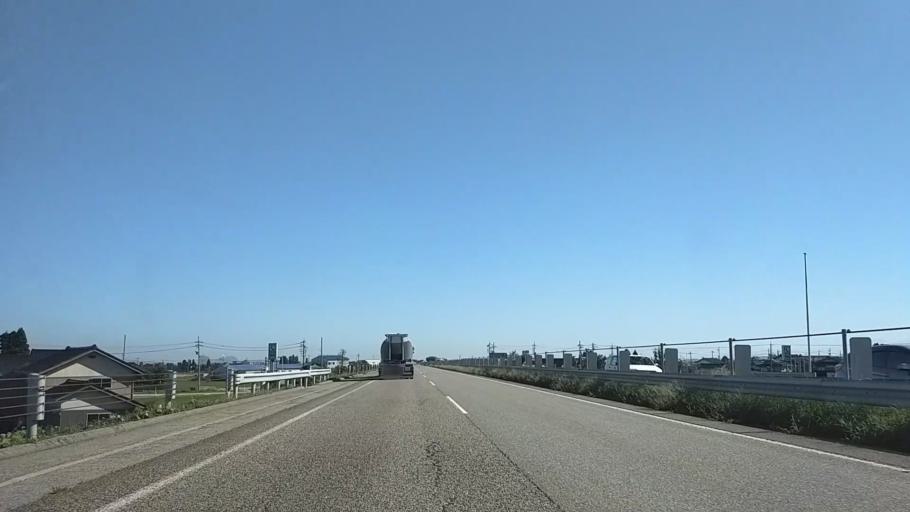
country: JP
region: Toyama
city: Nanto-shi
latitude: 36.6354
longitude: 136.9692
